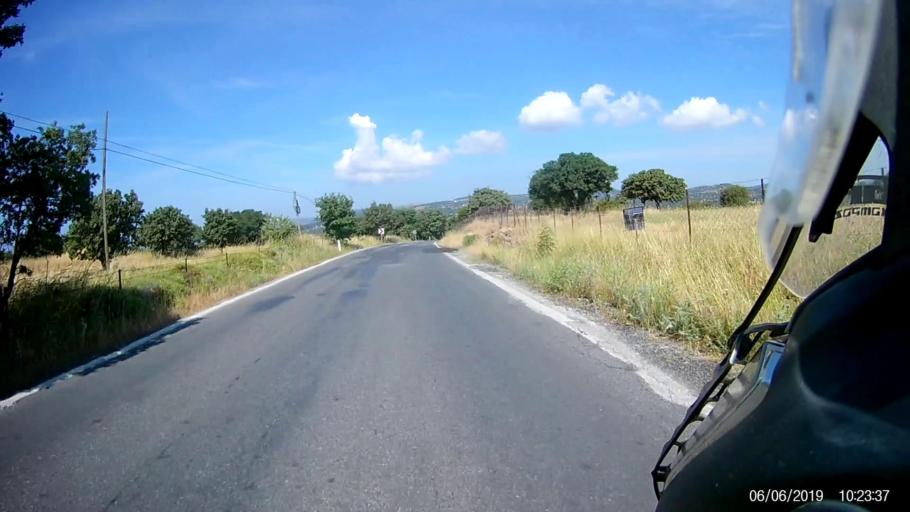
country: TR
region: Canakkale
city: Behram
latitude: 39.5069
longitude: 26.4205
